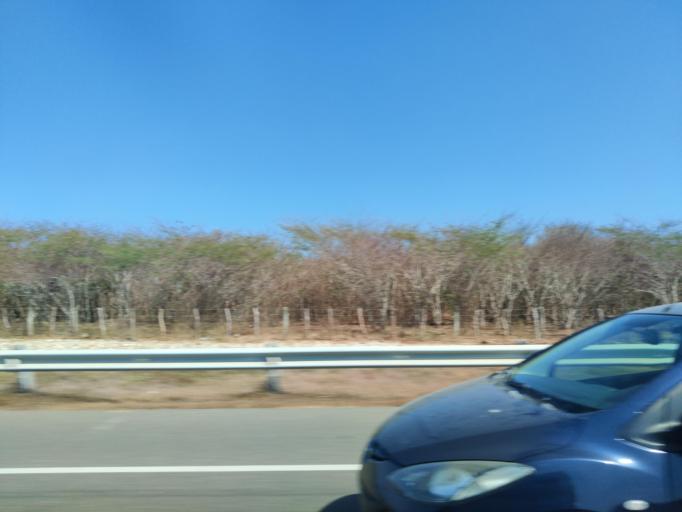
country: CO
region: Atlantico
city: Puerto Colombia
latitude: 10.9685
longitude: -74.9903
